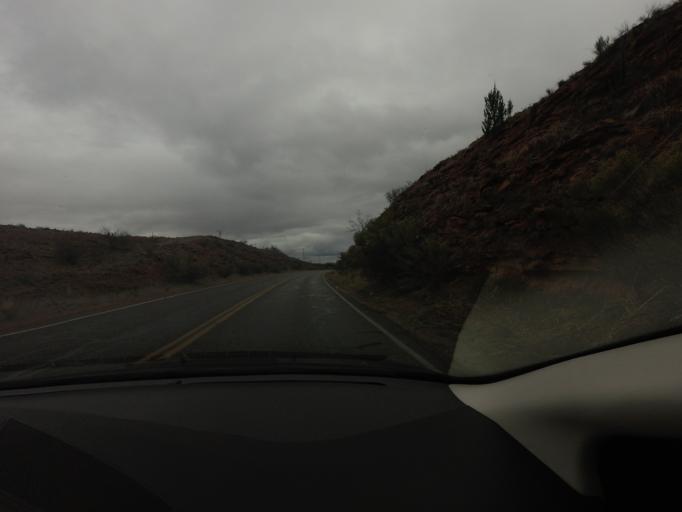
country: US
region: Arizona
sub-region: Yavapai County
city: Clarkdale
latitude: 34.7623
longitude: -112.0401
